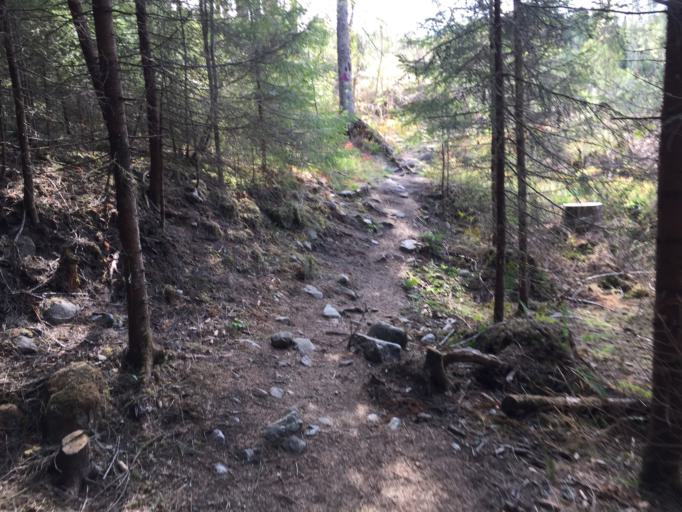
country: NO
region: Akershus
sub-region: Skedsmo
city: Lillestrom
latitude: 59.9266
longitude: 11.0206
